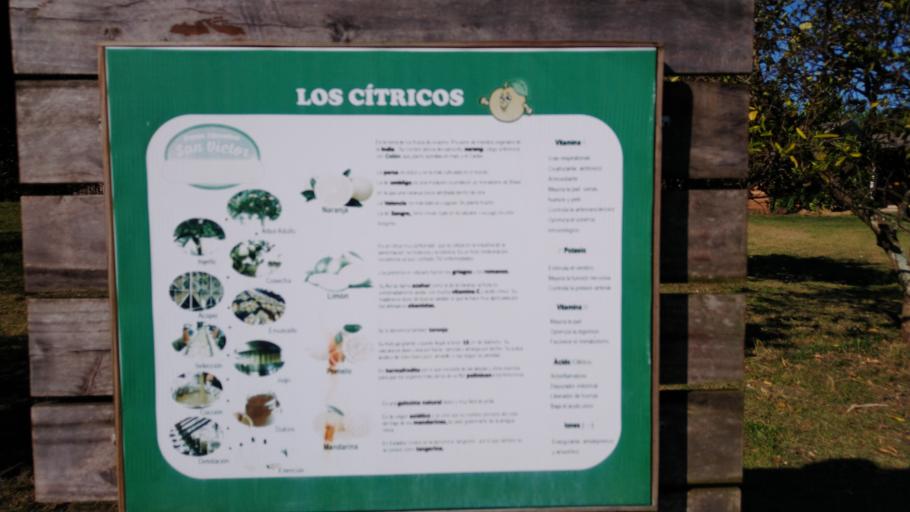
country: AR
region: Misiones
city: Garupa
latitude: -27.4914
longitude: -55.8209
